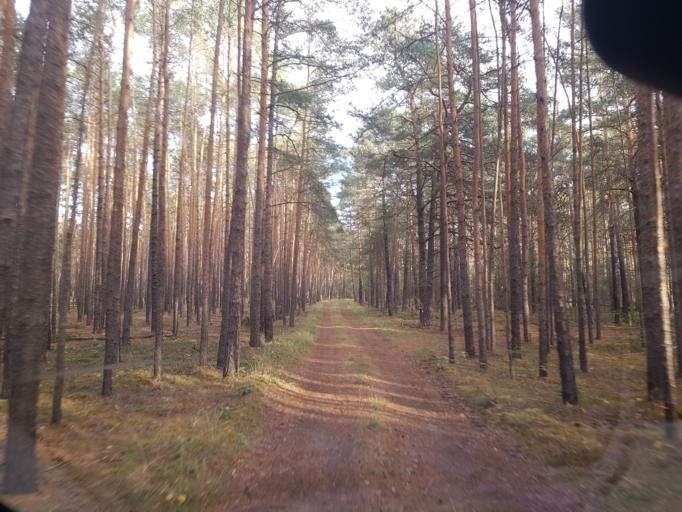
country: DE
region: Brandenburg
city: Finsterwalde
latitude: 51.5531
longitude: 13.6886
